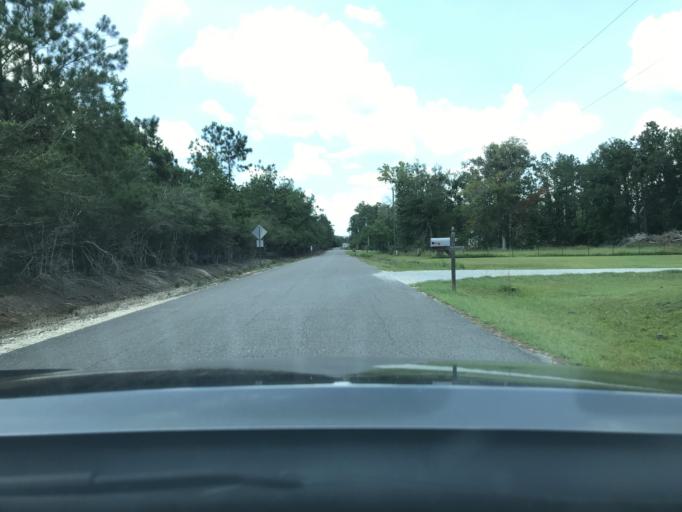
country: US
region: Louisiana
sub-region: Calcasieu Parish
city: Moss Bluff
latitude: 30.3307
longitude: -93.1308
